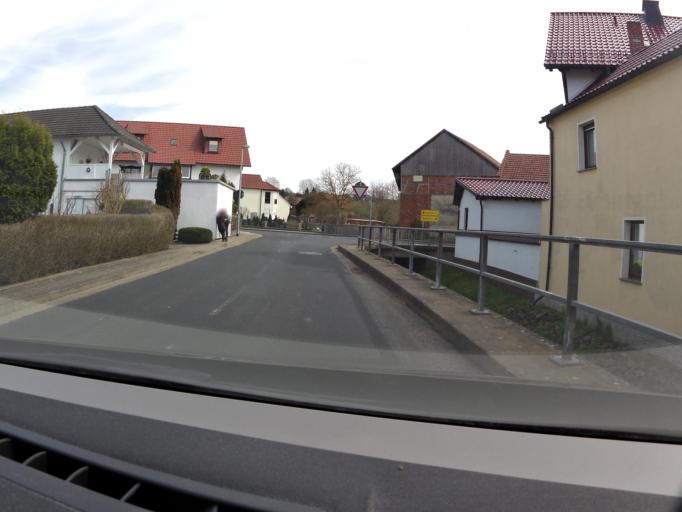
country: DE
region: Thuringia
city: Marksuhl
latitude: 50.8812
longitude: 10.2298
